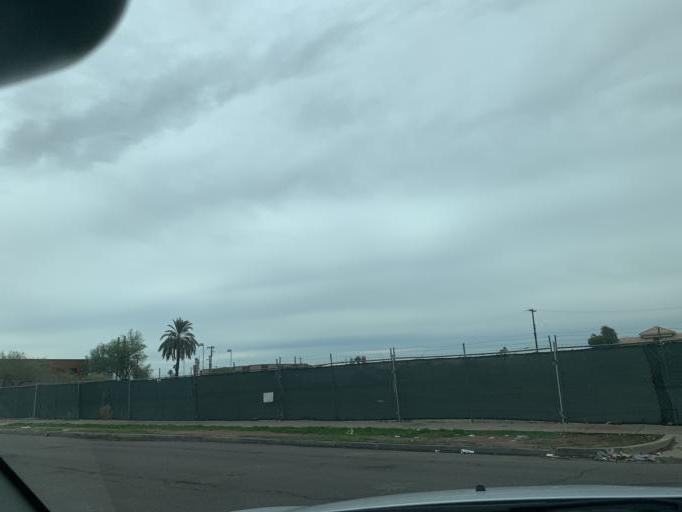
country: US
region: Arizona
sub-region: Maricopa County
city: Phoenix
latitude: 33.4530
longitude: -112.0605
